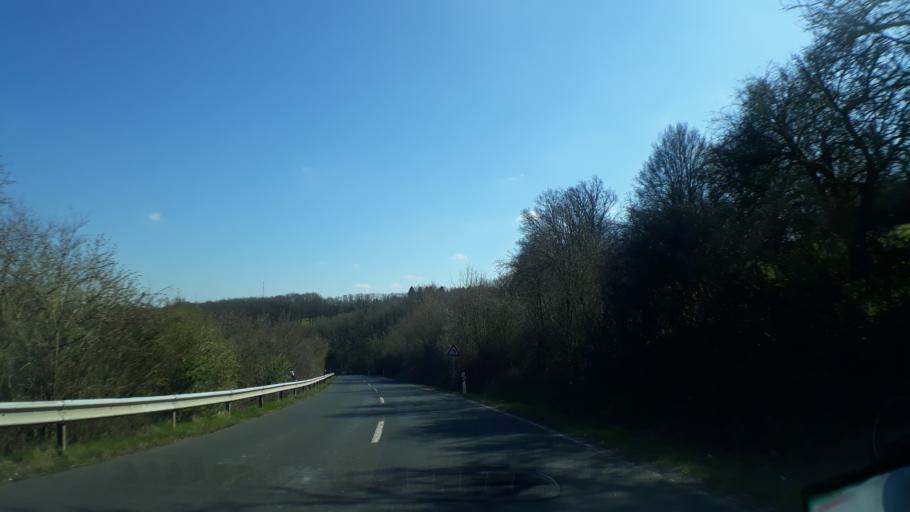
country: DE
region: North Rhine-Westphalia
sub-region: Regierungsbezirk Koln
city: Mechernich
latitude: 50.5643
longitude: 6.6493
